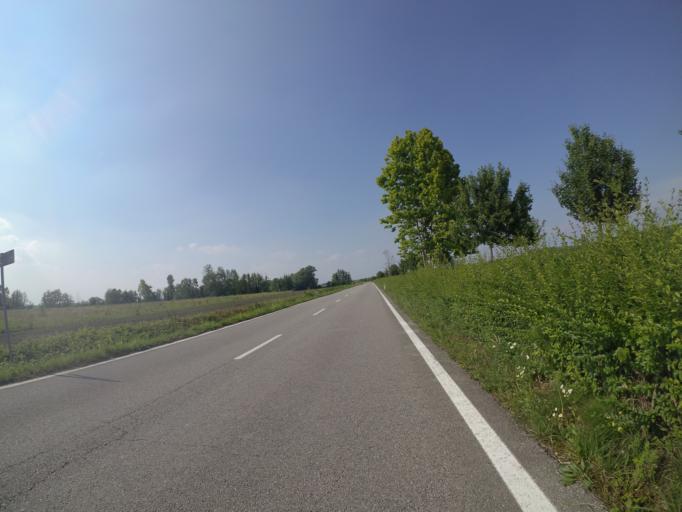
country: IT
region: Friuli Venezia Giulia
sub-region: Provincia di Udine
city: Camino al Tagliamento
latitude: 45.9215
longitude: 12.9640
